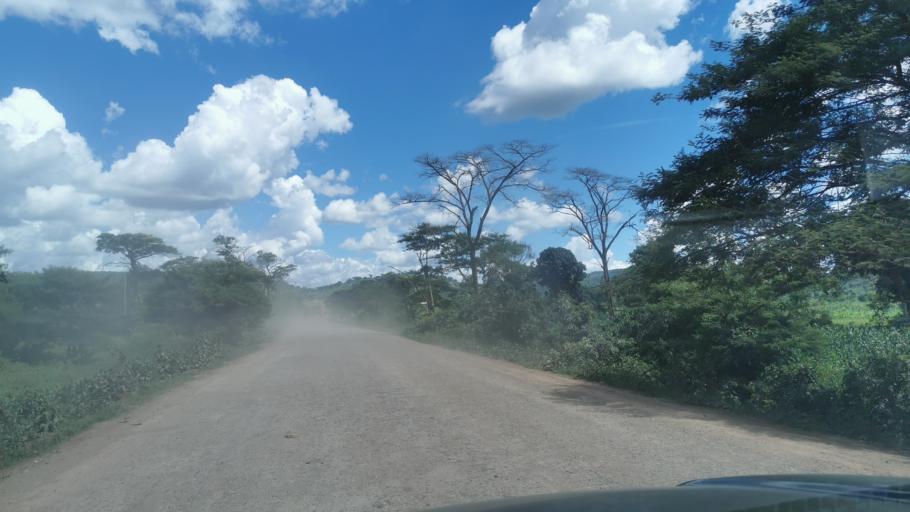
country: TZ
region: Kagera
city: Biharamulo
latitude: -2.8901
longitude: 31.1418
